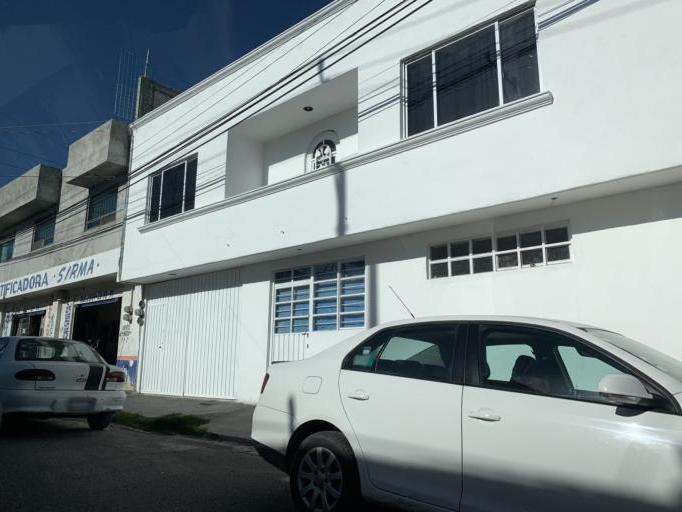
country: MX
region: Puebla
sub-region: Puebla
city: El Capulo (La Quebradora)
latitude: 18.9589
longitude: -98.2436
